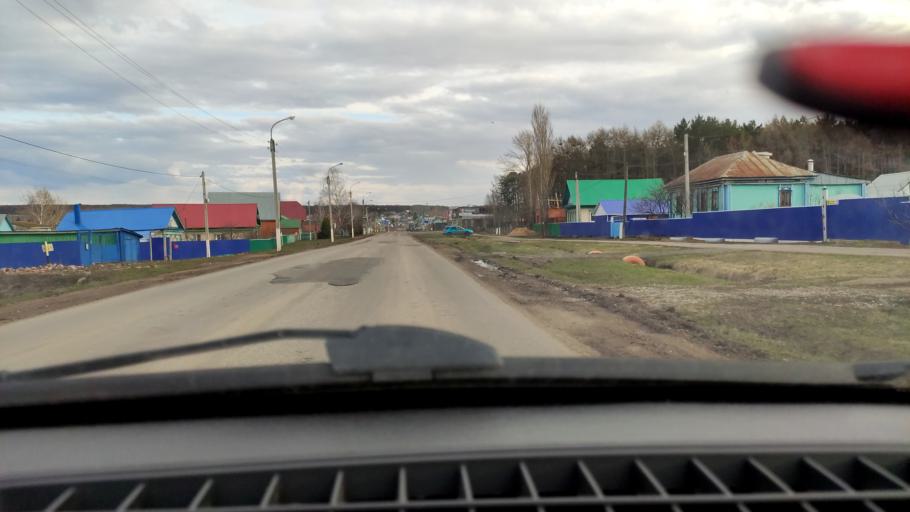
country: RU
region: Bashkortostan
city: Tolbazy
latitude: 54.0278
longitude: 55.8843
